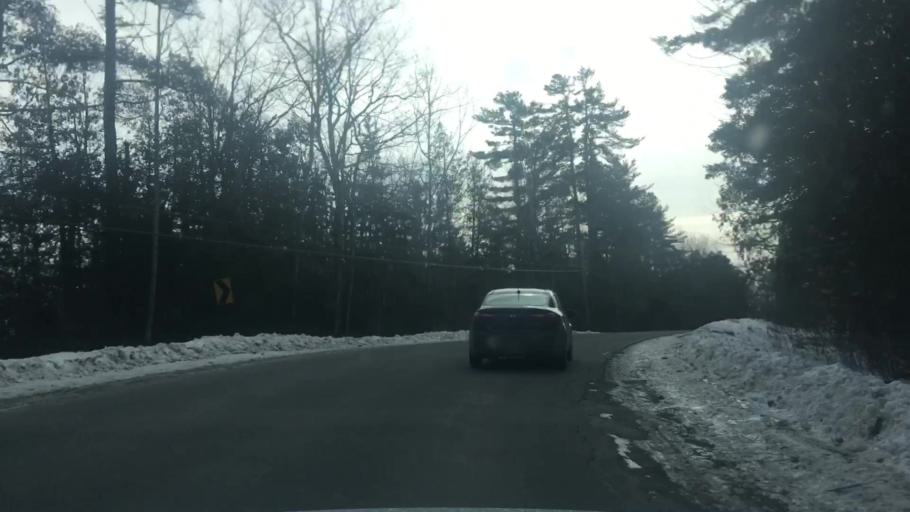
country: US
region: Maine
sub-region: Hancock County
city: Orland
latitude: 44.6275
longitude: -68.6984
